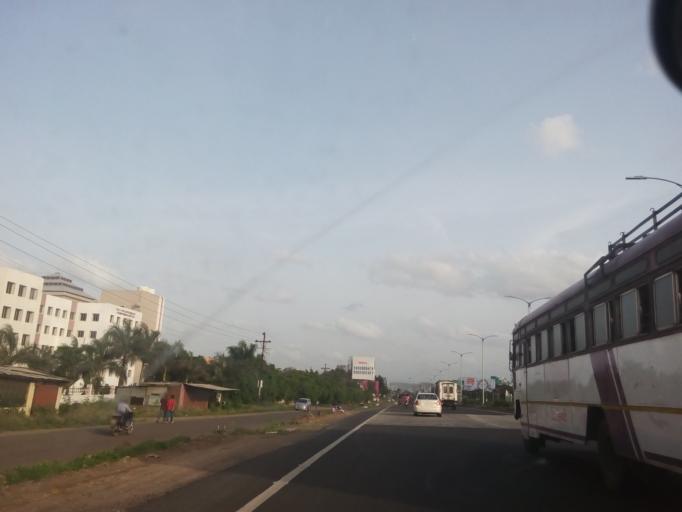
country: IN
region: Maharashtra
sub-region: Pune Division
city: Pimpri
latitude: 18.6152
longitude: 73.7486
